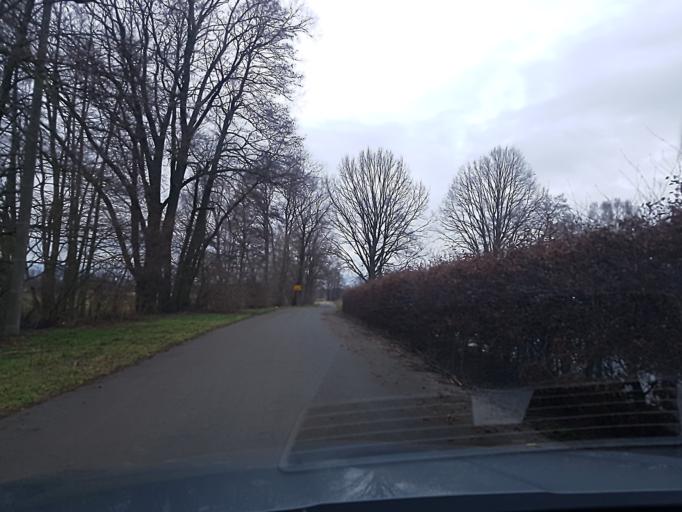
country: DE
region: Brandenburg
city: Schilda
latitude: 51.6222
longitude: 13.3539
